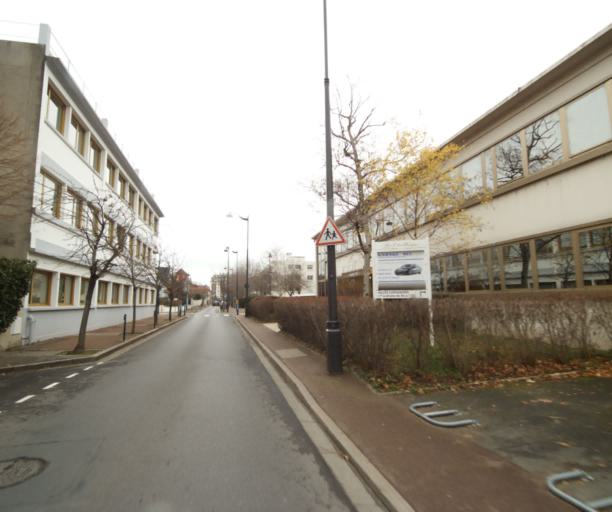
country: FR
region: Ile-de-France
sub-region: Departement des Hauts-de-Seine
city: Rueil-Malmaison
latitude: 48.8811
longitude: 2.1741
